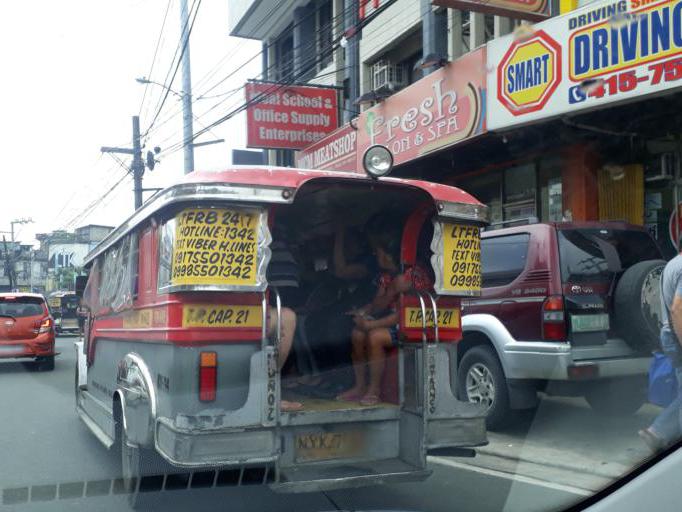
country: PH
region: Calabarzon
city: Del Monte
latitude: 14.6403
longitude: 121.0163
